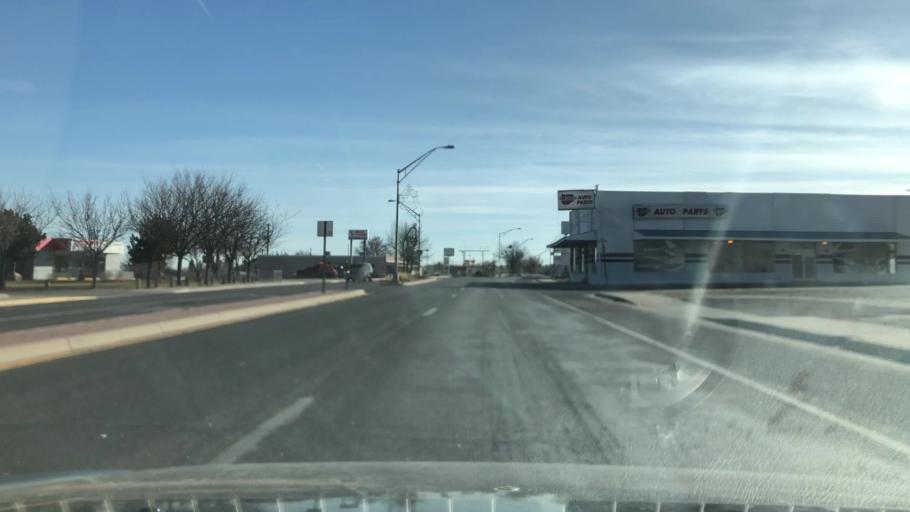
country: US
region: New Mexico
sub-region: Socorro County
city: Socorro
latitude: 34.0573
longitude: -106.8917
